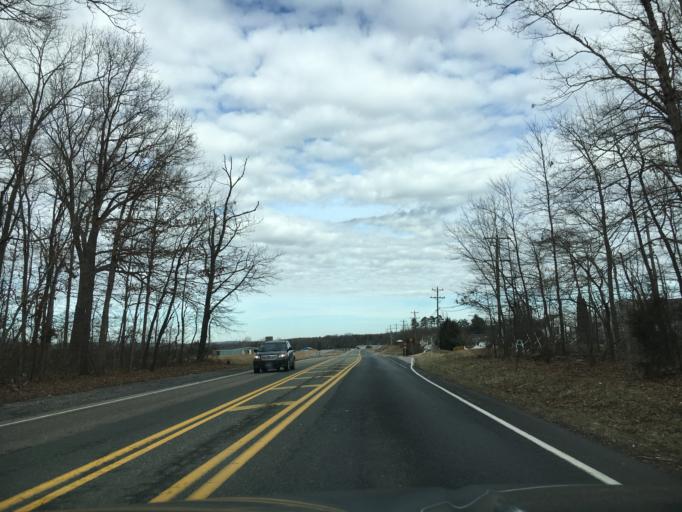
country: US
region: Virginia
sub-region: Augusta County
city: Crimora
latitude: 38.1342
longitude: -78.8453
